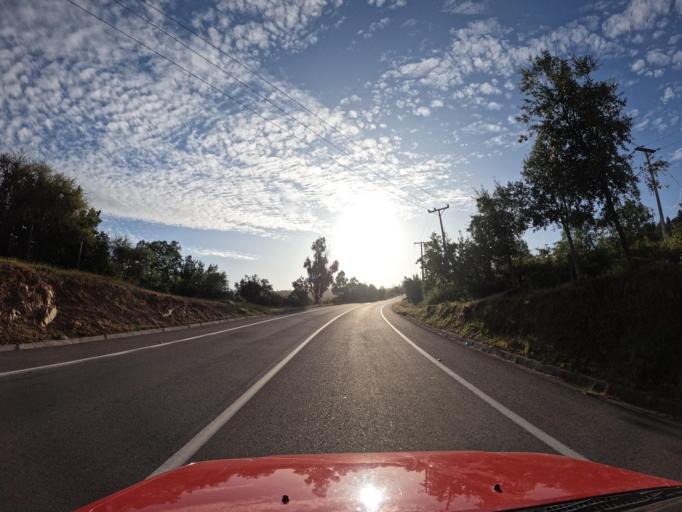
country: CL
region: Valparaiso
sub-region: San Antonio Province
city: San Antonio
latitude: -34.0510
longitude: -71.6017
